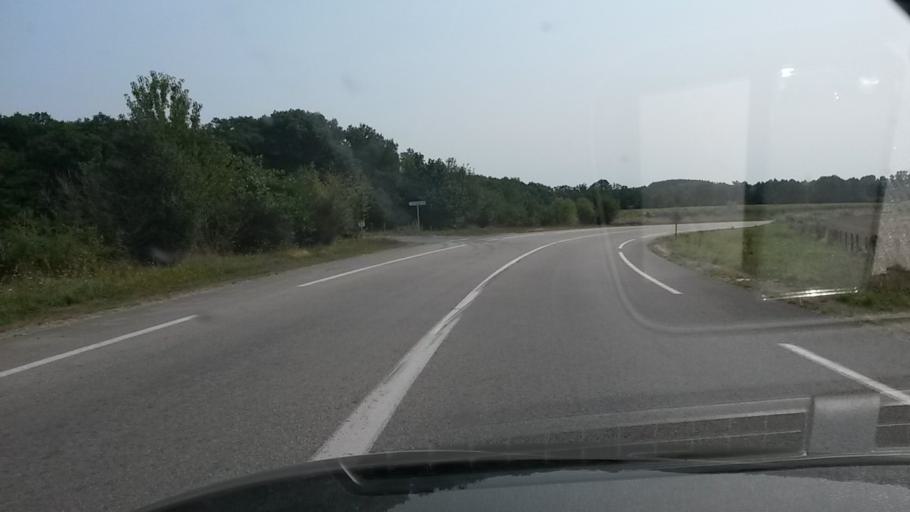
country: FR
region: Pays de la Loire
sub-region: Departement de la Mayenne
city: Chemaze
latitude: 47.7942
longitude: -0.7617
